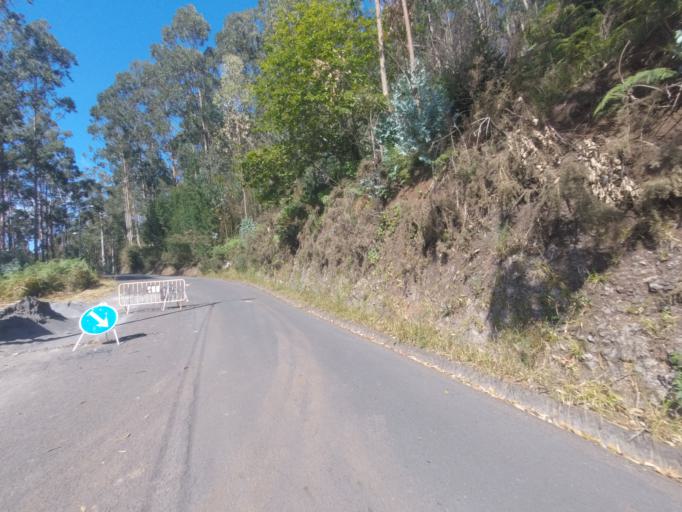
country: PT
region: Madeira
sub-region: Ribeira Brava
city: Campanario
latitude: 32.6870
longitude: -17.0218
